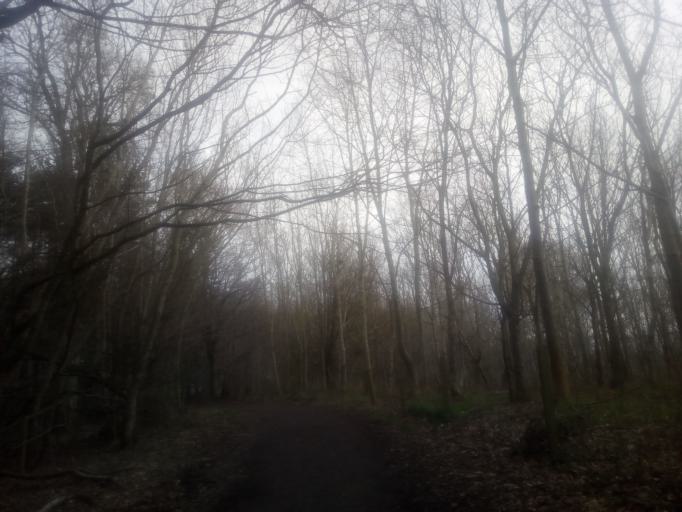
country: GB
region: Scotland
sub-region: The Scottish Borders
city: Saint Boswells
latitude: 55.5863
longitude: -2.6475
